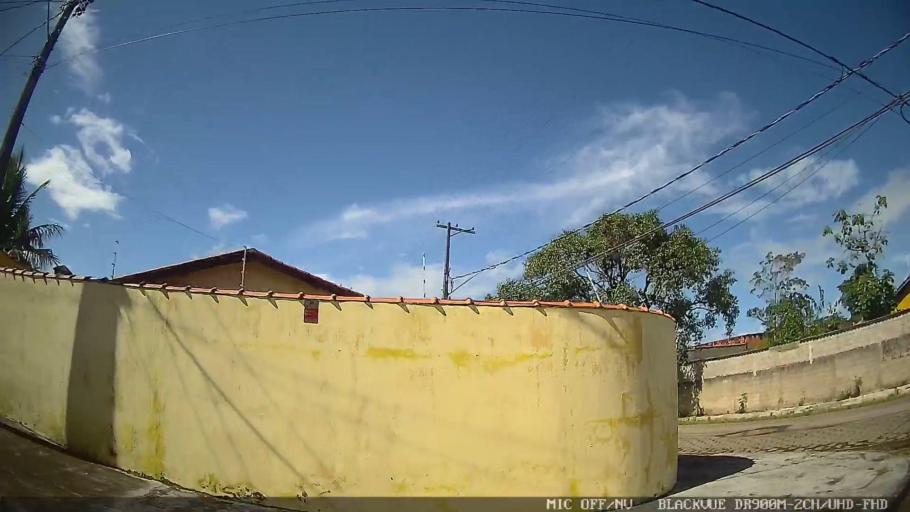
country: BR
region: Sao Paulo
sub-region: Itanhaem
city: Itanhaem
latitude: -24.2371
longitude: -46.8841
